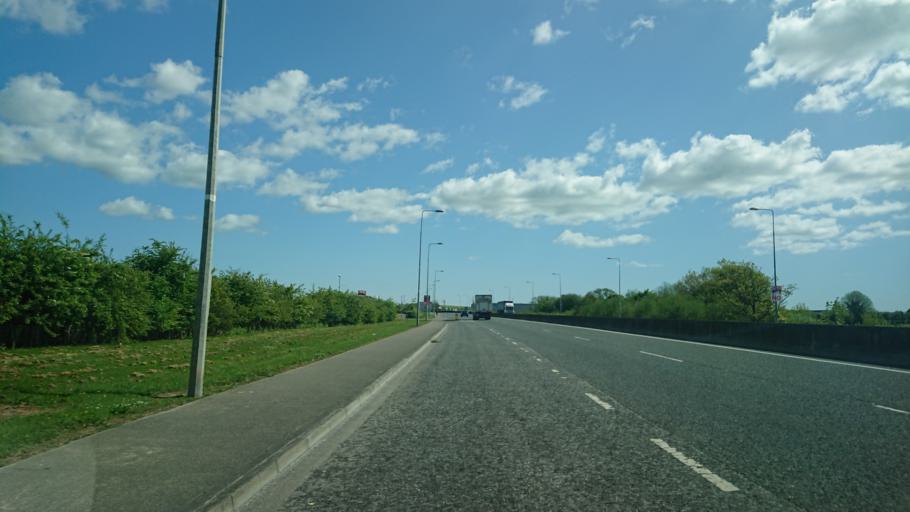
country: IE
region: Munster
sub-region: Waterford
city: Waterford
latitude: 52.2457
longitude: -7.1716
